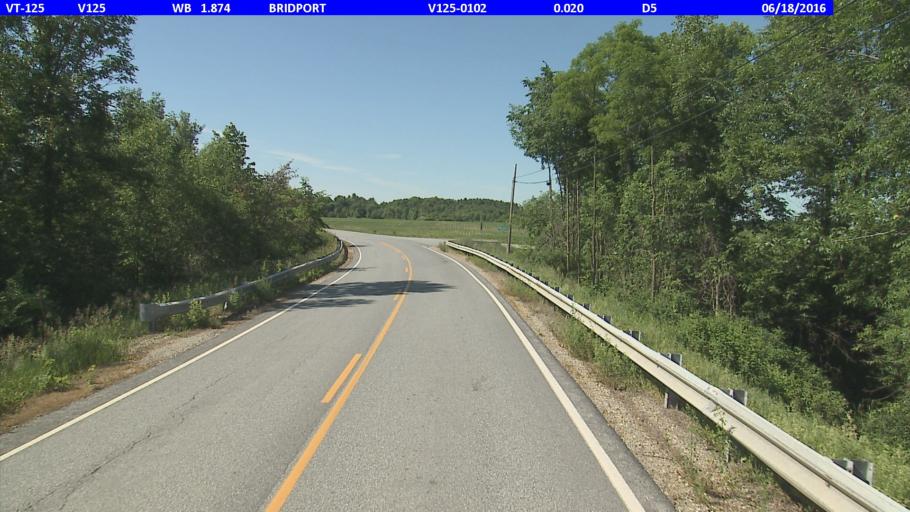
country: US
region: New York
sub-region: Essex County
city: Port Henry
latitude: 44.0217
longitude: -73.3905
